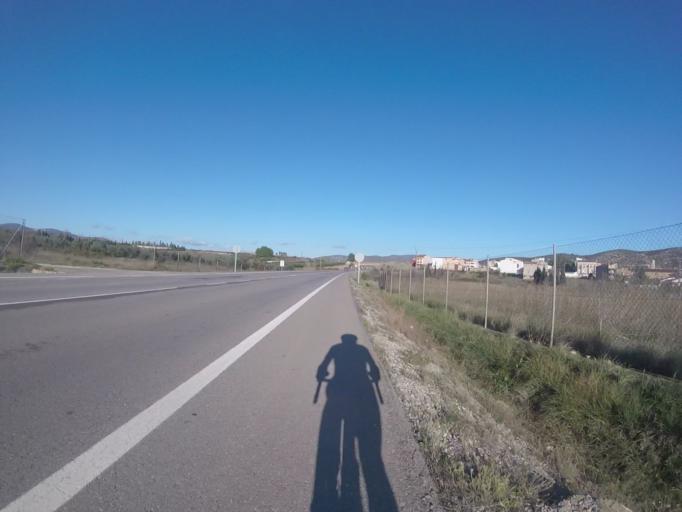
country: ES
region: Valencia
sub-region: Provincia de Castello
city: Cuevas de Vinroma
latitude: 40.3092
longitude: 0.1149
